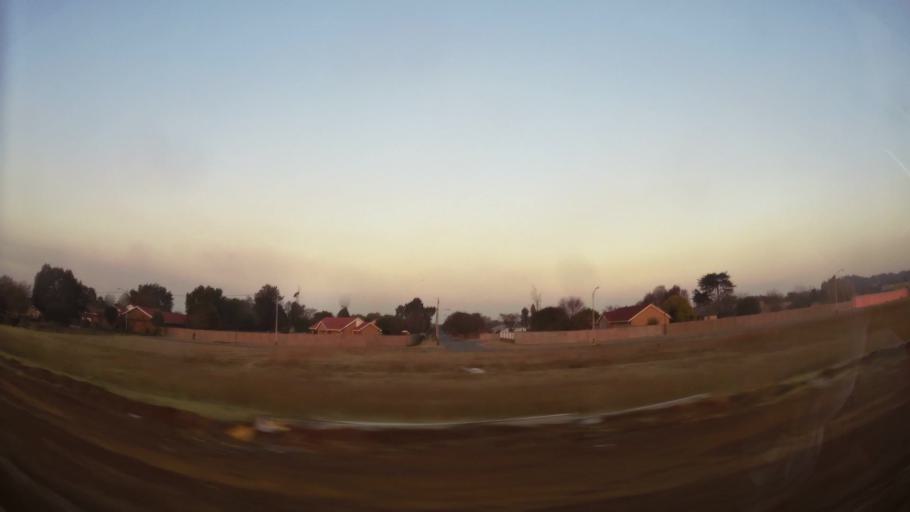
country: ZA
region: Gauteng
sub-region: Ekurhuleni Metropolitan Municipality
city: Springs
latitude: -26.3445
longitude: 28.4168
